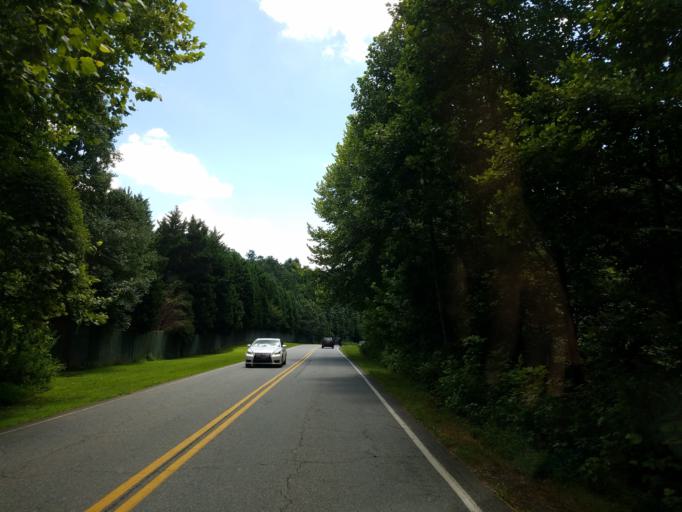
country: US
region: Georgia
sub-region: Fulton County
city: Alpharetta
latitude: 34.0991
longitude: -84.2238
